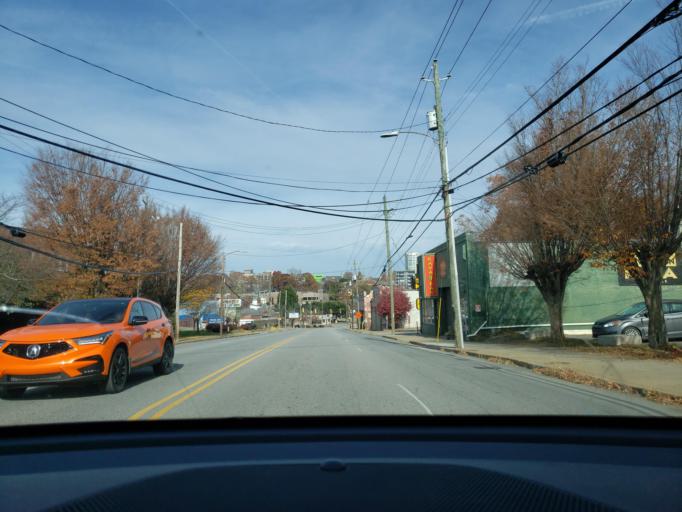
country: US
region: North Carolina
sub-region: Buncombe County
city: Asheville
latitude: 35.5850
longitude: -82.5514
